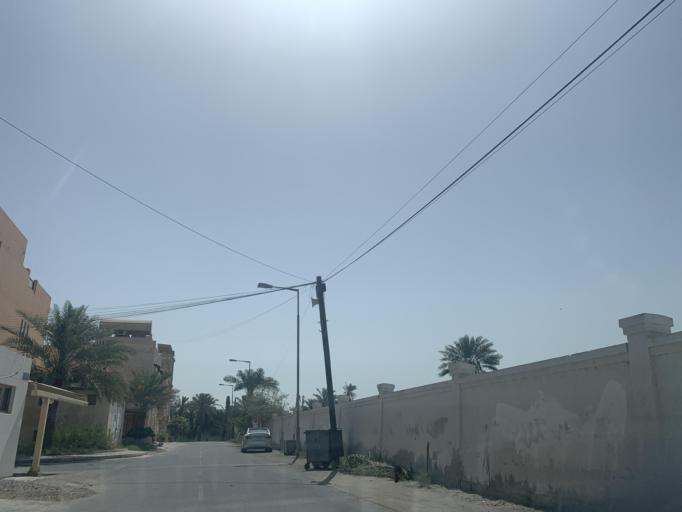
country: BH
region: Manama
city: Jidd Hafs
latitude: 26.2026
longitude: 50.5550
